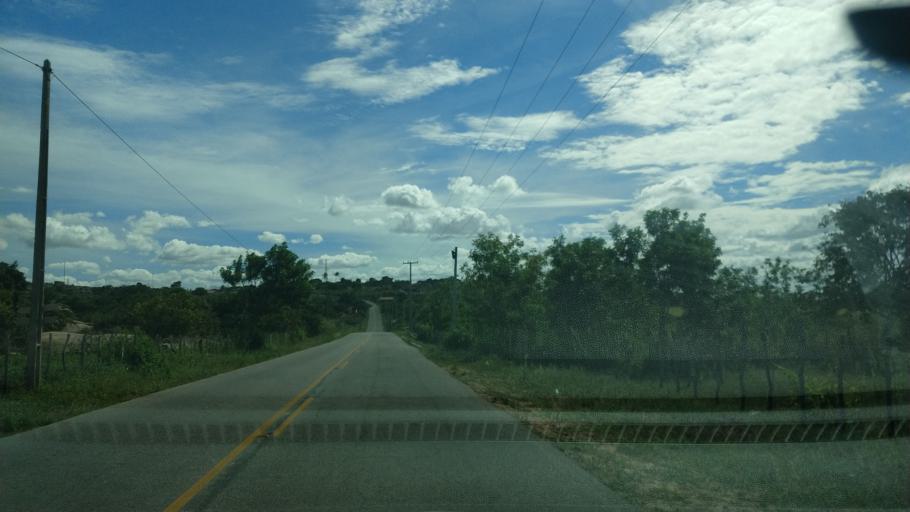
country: BR
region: Rio Grande do Norte
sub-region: Sao Jose Do Campestre
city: Sao Jose do Campestre
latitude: -6.4195
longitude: -35.7225
